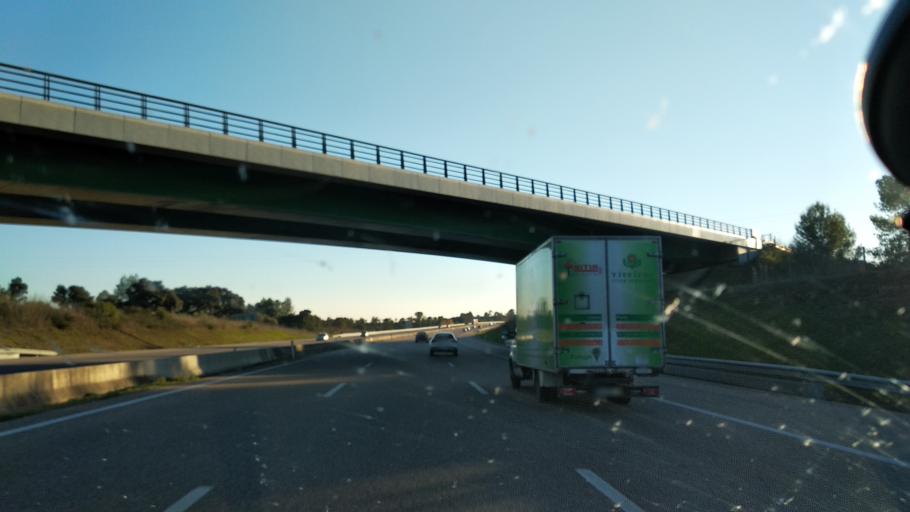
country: PT
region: Santarem
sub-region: Alcanena
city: Alcanena
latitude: 39.4352
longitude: -8.6276
